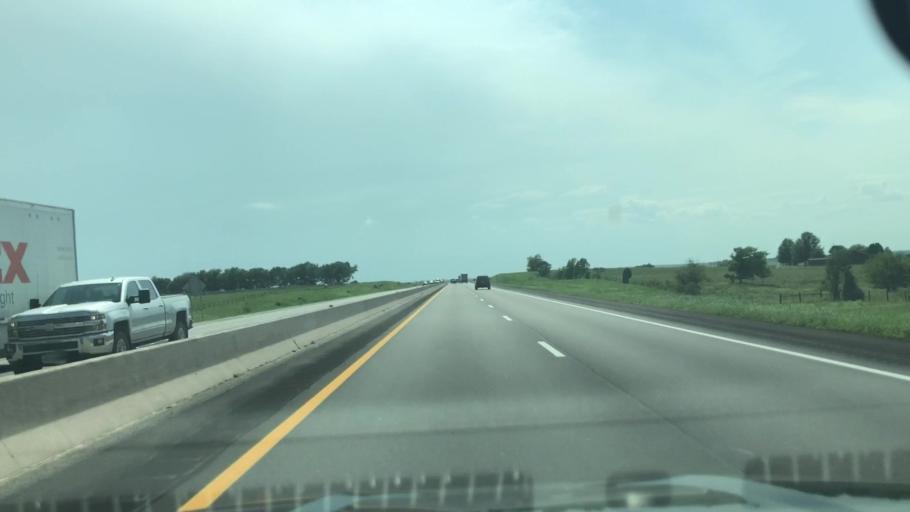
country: US
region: Oklahoma
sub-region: Ottawa County
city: Afton
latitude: 36.6984
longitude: -94.9997
